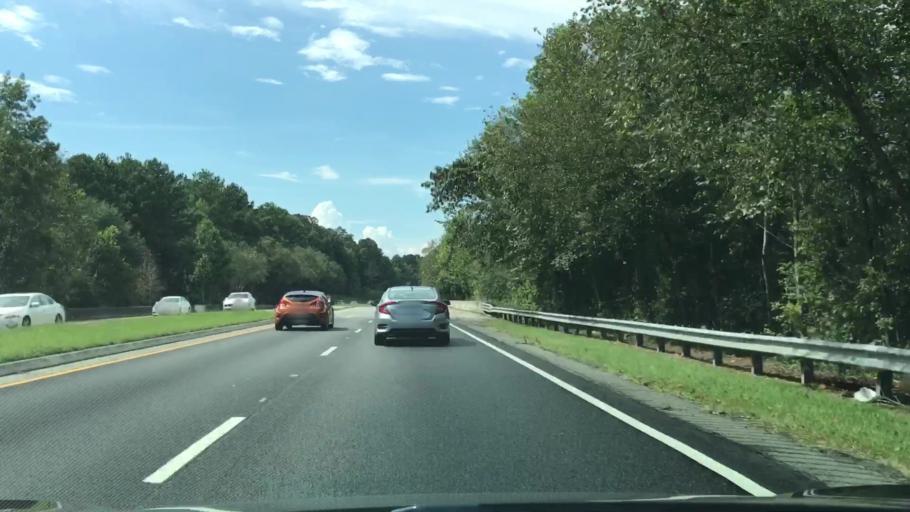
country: US
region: Georgia
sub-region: Gwinnett County
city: Snellville
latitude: 33.8989
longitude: -84.0727
